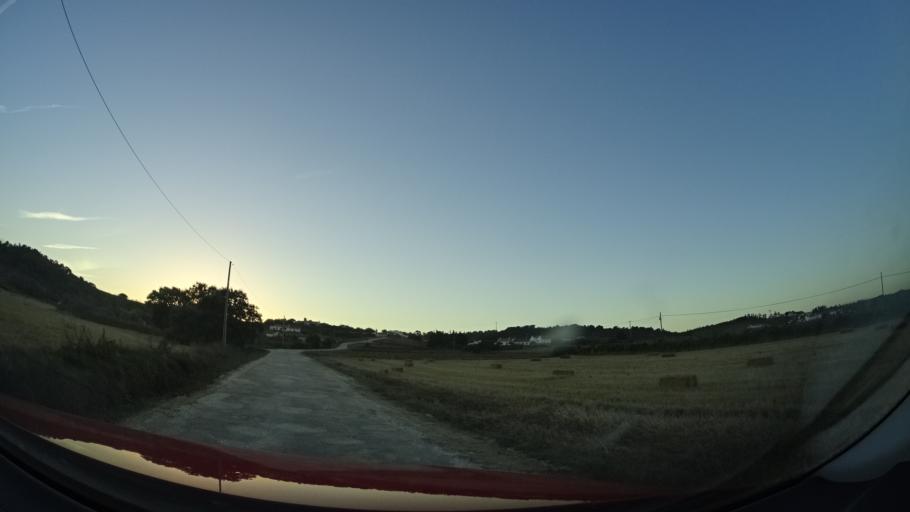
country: PT
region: Faro
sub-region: Aljezur
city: Aljezur
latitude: 37.2377
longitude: -8.8285
